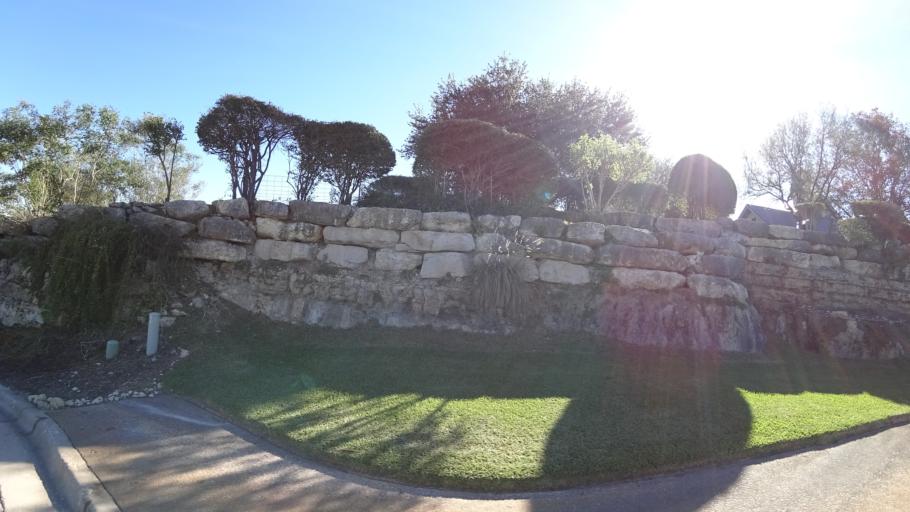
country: US
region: Texas
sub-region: Travis County
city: West Lake Hills
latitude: 30.3327
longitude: -97.7969
